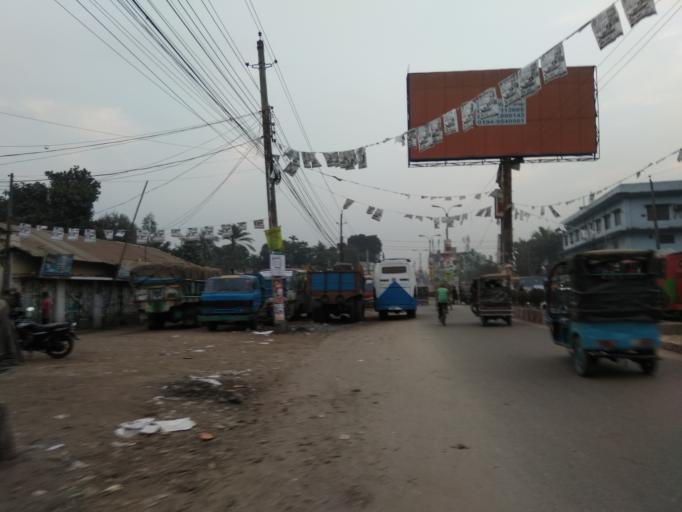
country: BD
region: Rangpur Division
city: Rangpur
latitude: 25.7347
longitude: 89.2548
